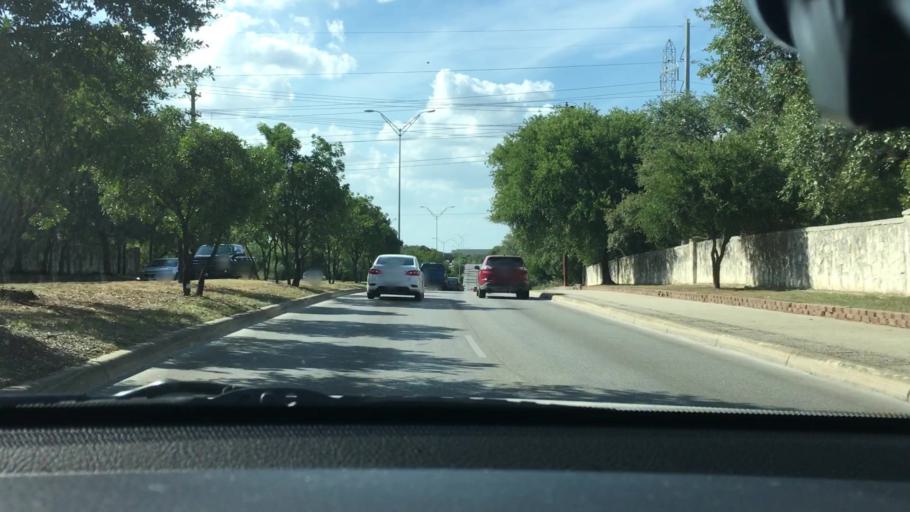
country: US
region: Texas
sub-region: Bexar County
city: Selma
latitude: 29.5846
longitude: -98.2864
